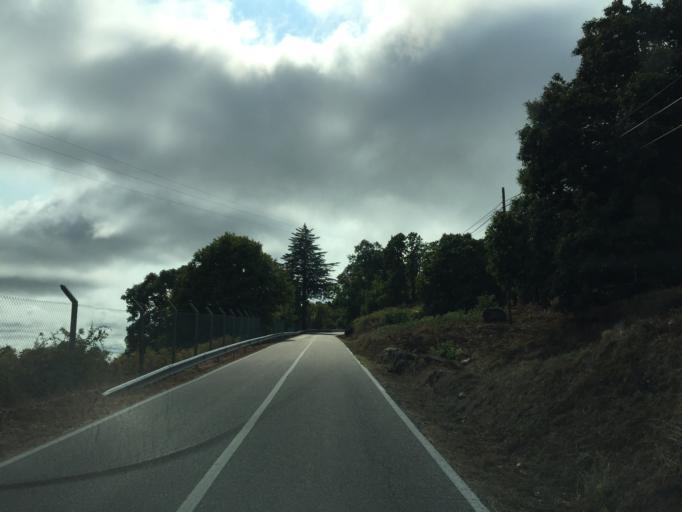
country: PT
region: Portalegre
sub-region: Marvao
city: Marvao
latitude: 39.4016
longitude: -7.3809
